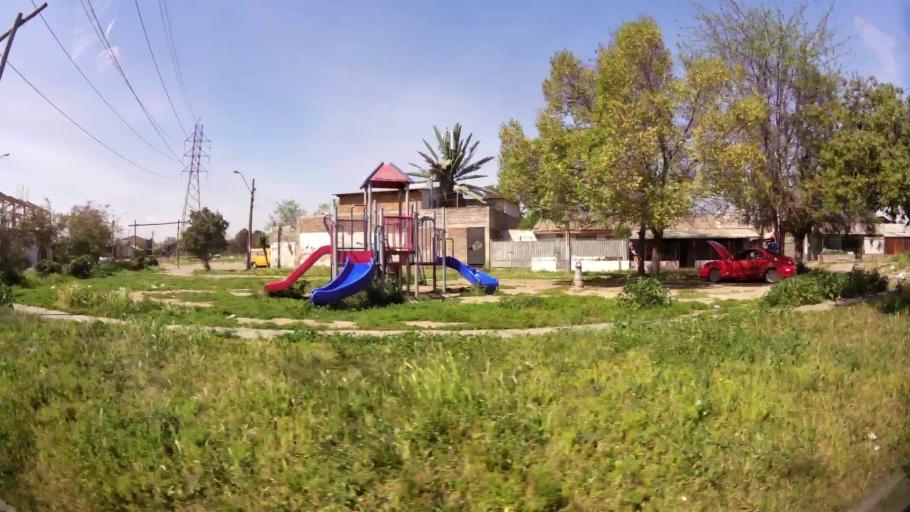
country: CL
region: Santiago Metropolitan
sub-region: Provincia de Maipo
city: San Bernardo
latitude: -33.5271
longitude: -70.7037
